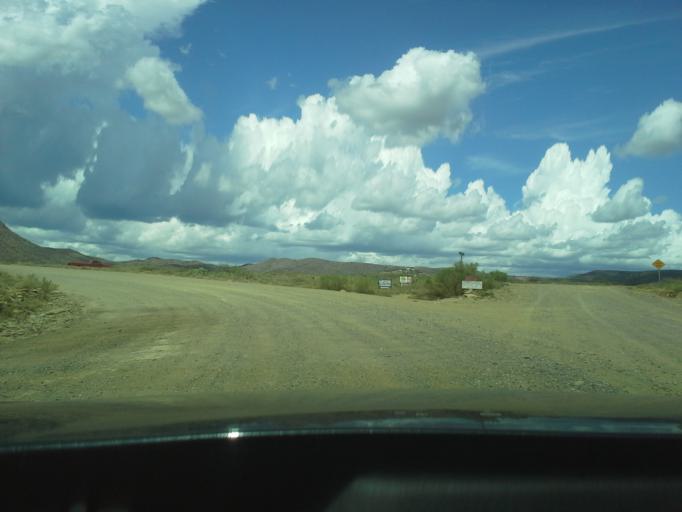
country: US
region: Arizona
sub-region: Yavapai County
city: Spring Valley
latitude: 34.2739
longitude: -112.1922
